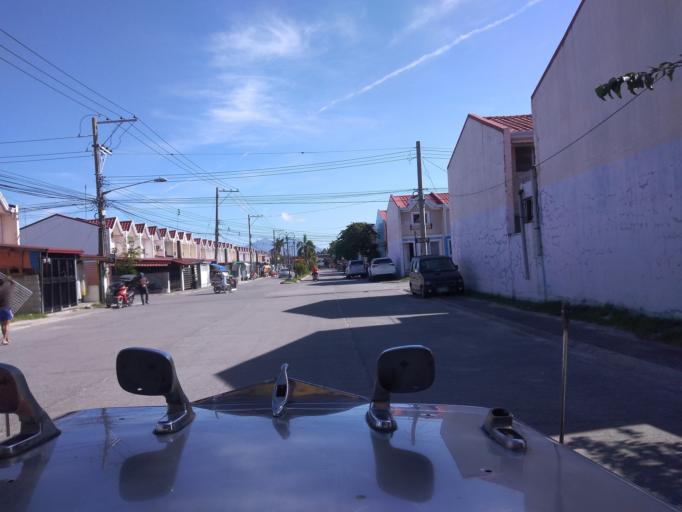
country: PH
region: Central Luzon
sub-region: Province of Pampanga
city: Calibutbut
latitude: 15.0986
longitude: 120.6008
